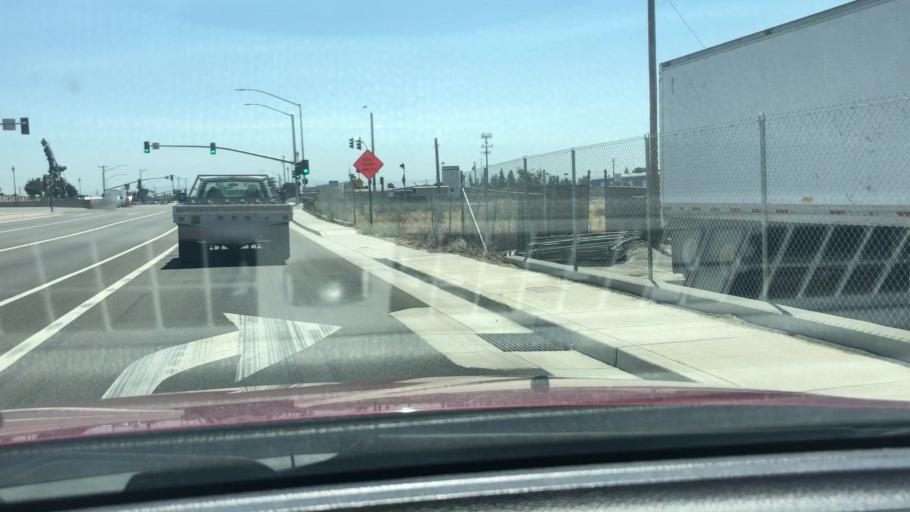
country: US
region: California
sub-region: Stanislaus County
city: Salida
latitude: 37.7100
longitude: -121.0799
